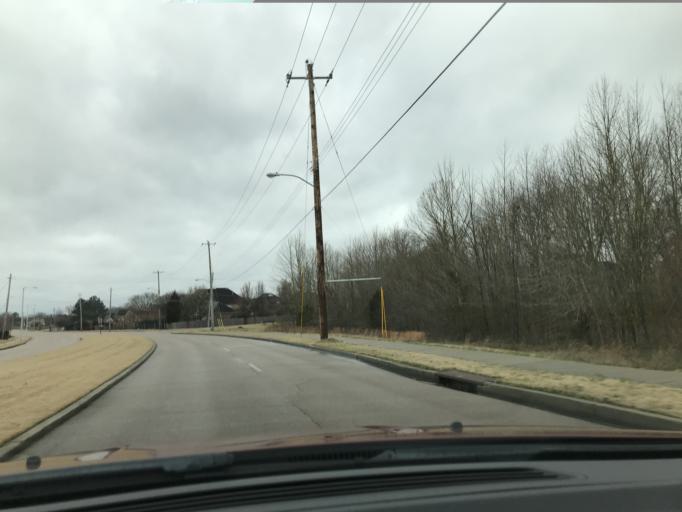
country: US
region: Tennessee
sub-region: Shelby County
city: Collierville
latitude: 35.0803
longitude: -89.6847
